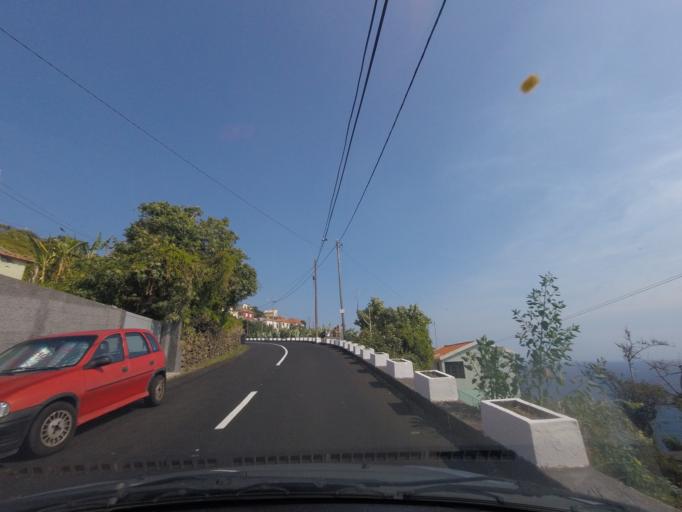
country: PT
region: Madeira
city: Ribeira Brava
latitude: 32.6703
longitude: -17.0595
